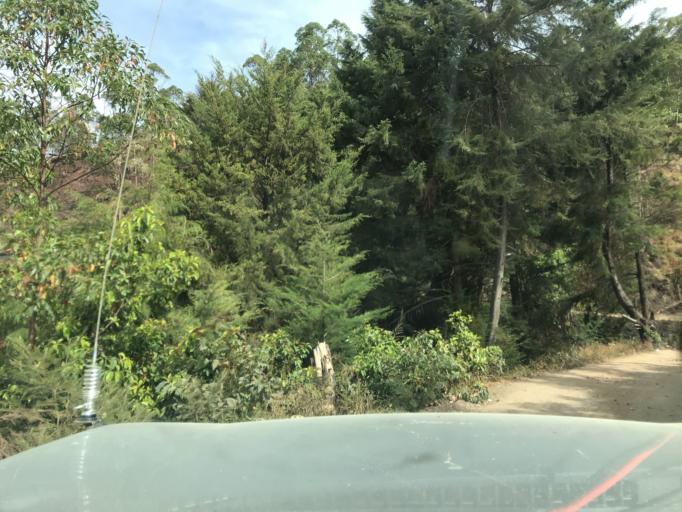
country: TL
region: Ainaro
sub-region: Ainaro
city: Ainaro
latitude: -8.8822
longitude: 125.5408
